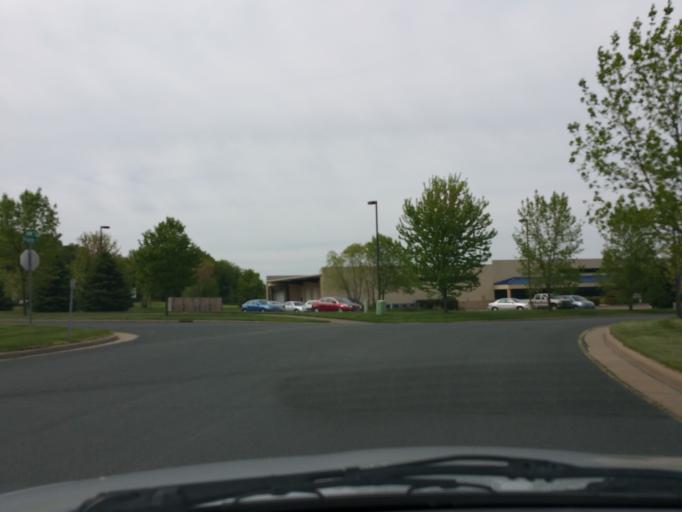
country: US
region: Wisconsin
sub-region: Pierce County
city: River Falls
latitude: 44.8899
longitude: -92.6367
